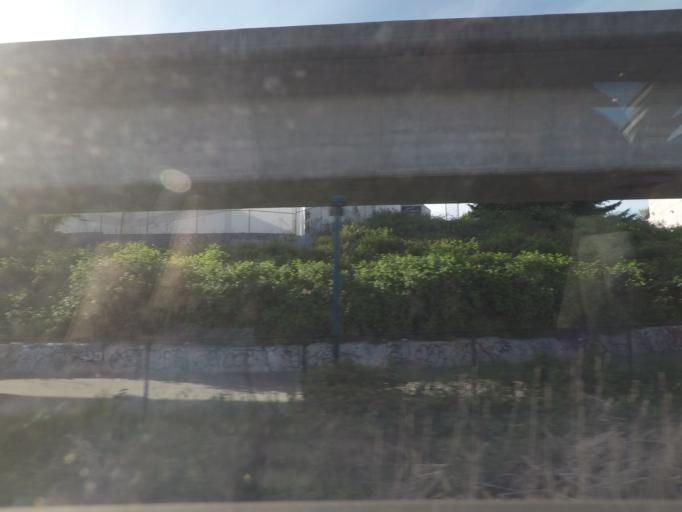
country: CA
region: British Columbia
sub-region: Fraser Valley Regional District
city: North Vancouver
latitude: 49.2611
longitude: -123.0313
